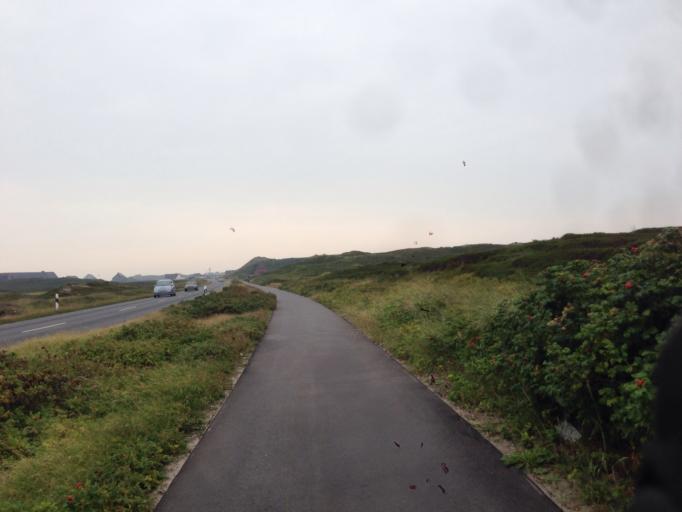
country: DE
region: Schleswig-Holstein
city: Norddorf
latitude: 54.7782
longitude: 8.2841
